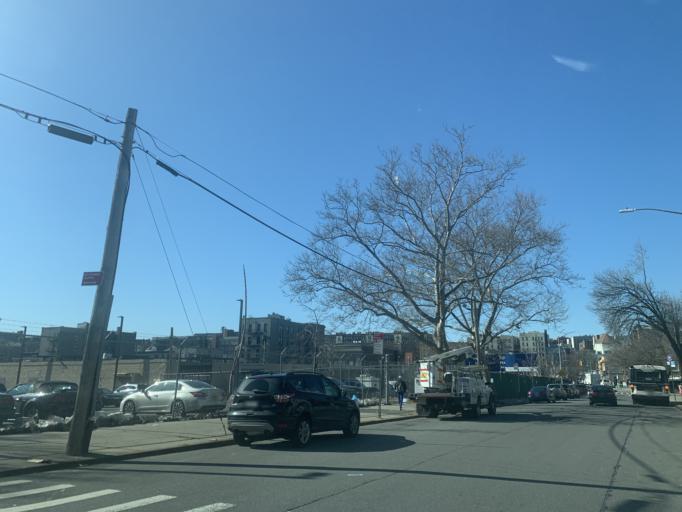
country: US
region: New York
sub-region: Bronx
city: The Bronx
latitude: 40.8594
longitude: -73.8905
